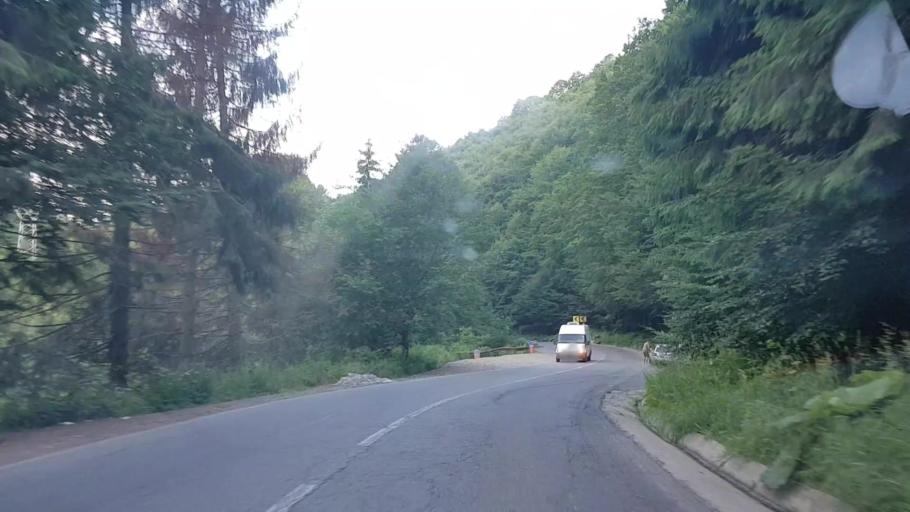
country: RO
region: Harghita
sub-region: Comuna Praid
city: Ocna de Sus
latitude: 46.5982
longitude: 25.2397
